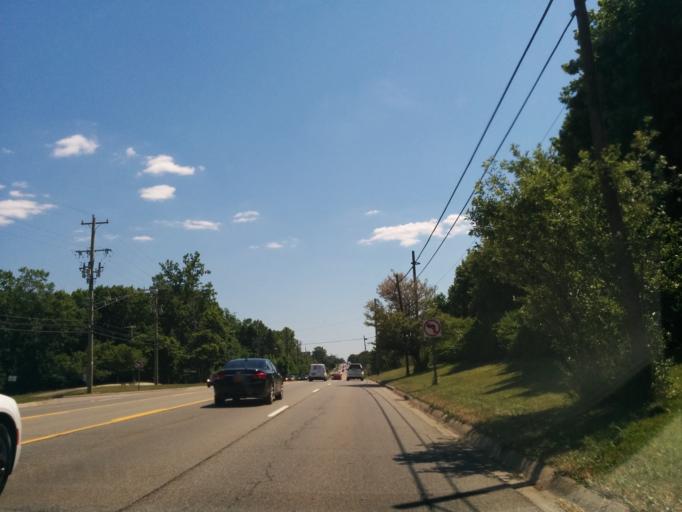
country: US
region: Michigan
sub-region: Oakland County
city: Orchard Lake
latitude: 42.5657
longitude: -83.3619
